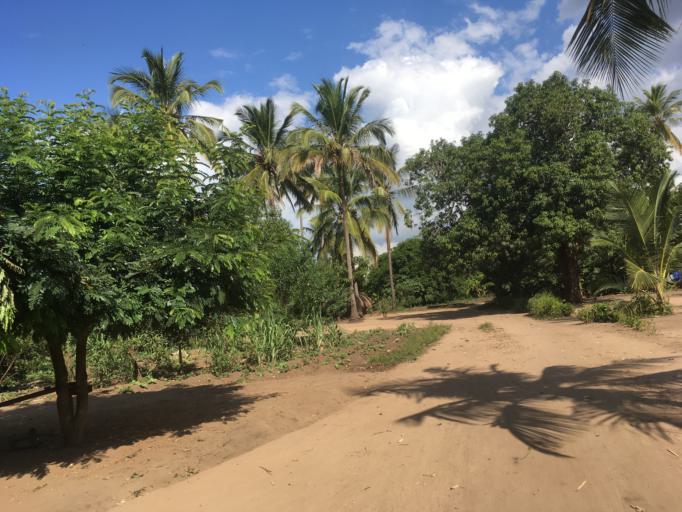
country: MZ
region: Zambezia
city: Quelimane
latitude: -17.6446
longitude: 36.6858
